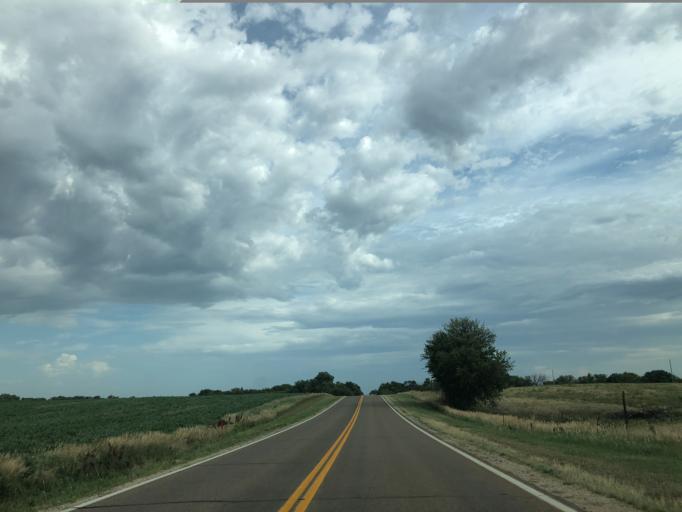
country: US
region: Kansas
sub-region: Ellsworth County
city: Ellsworth
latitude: 38.8126
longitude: -98.2249
